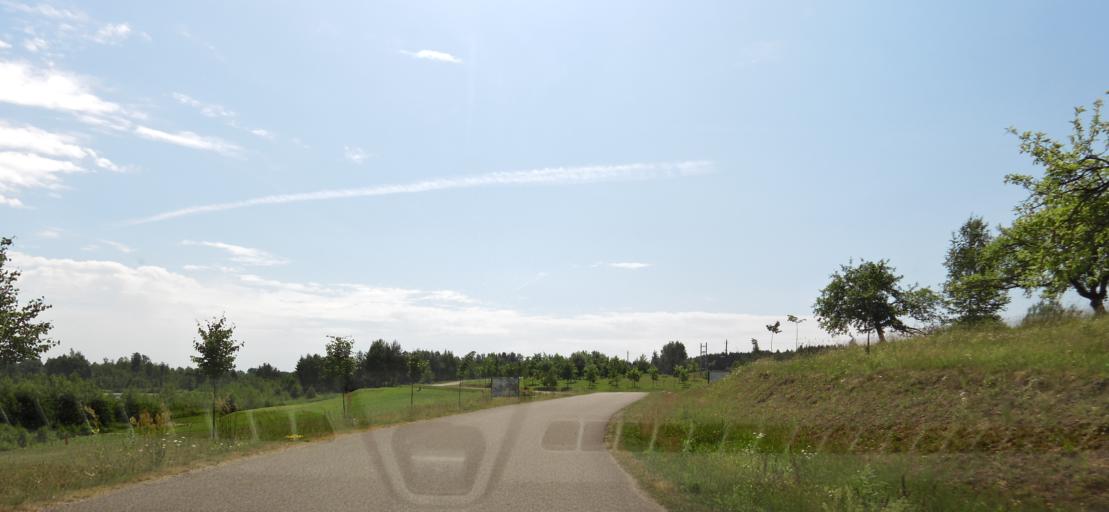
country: LT
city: Nemencine
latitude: 54.9102
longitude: 25.3156
